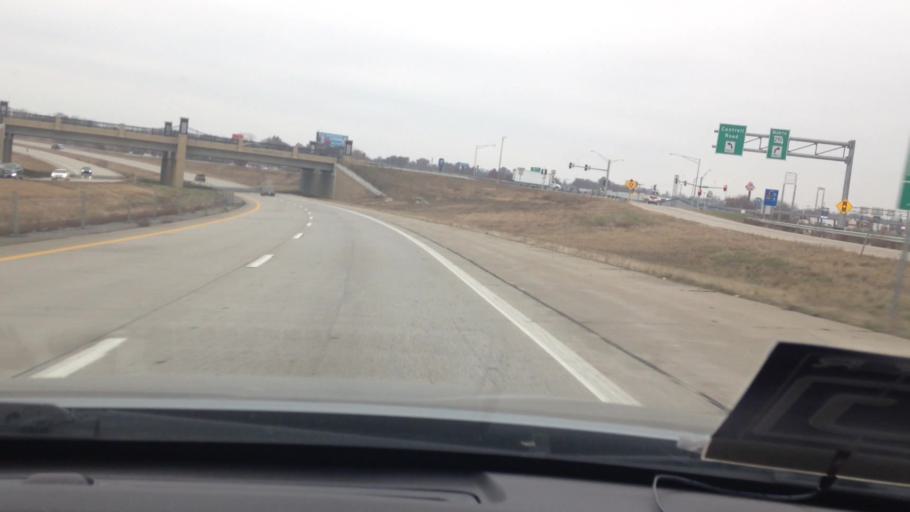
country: US
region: Missouri
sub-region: Cass County
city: Harrisonville
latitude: 38.6594
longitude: -94.3676
